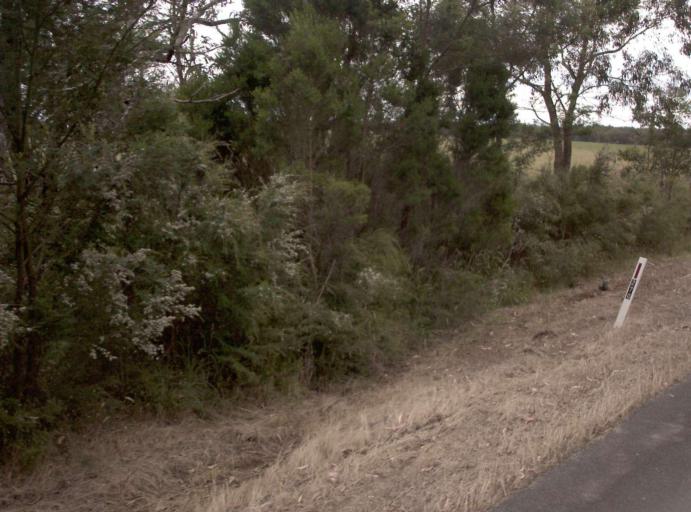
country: AU
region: Victoria
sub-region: Wellington
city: Sale
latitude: -38.2784
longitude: 147.0363
